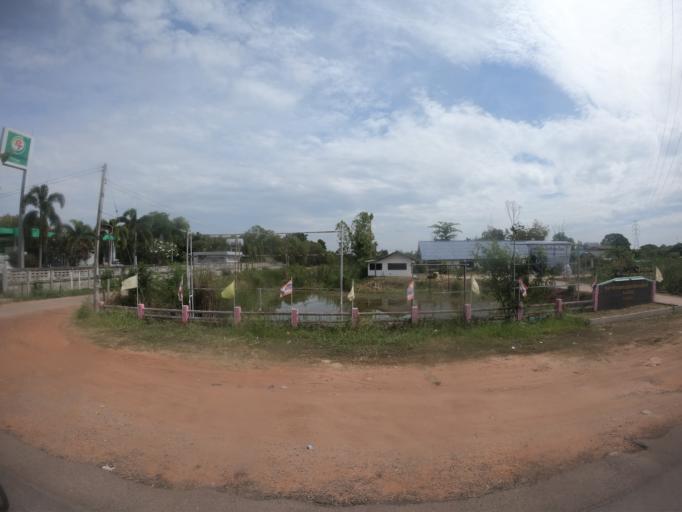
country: TH
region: Maha Sarakham
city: Chiang Yuen
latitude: 16.4022
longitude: 103.0996
